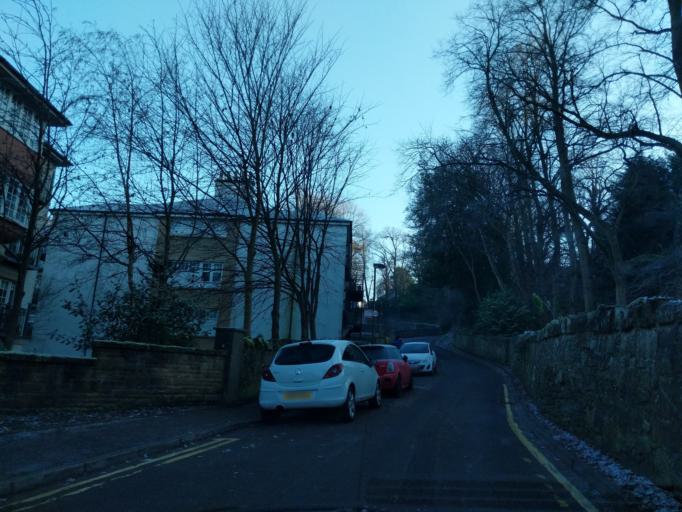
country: GB
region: Scotland
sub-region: Edinburgh
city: Colinton
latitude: 55.9052
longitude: -3.2637
